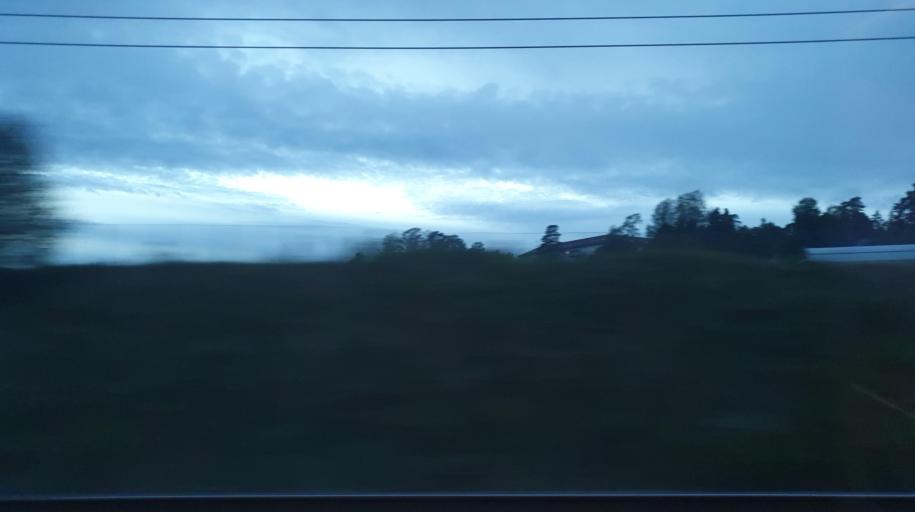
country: NO
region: Vestfold
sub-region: Sande
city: Sande
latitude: 59.5949
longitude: 10.2017
